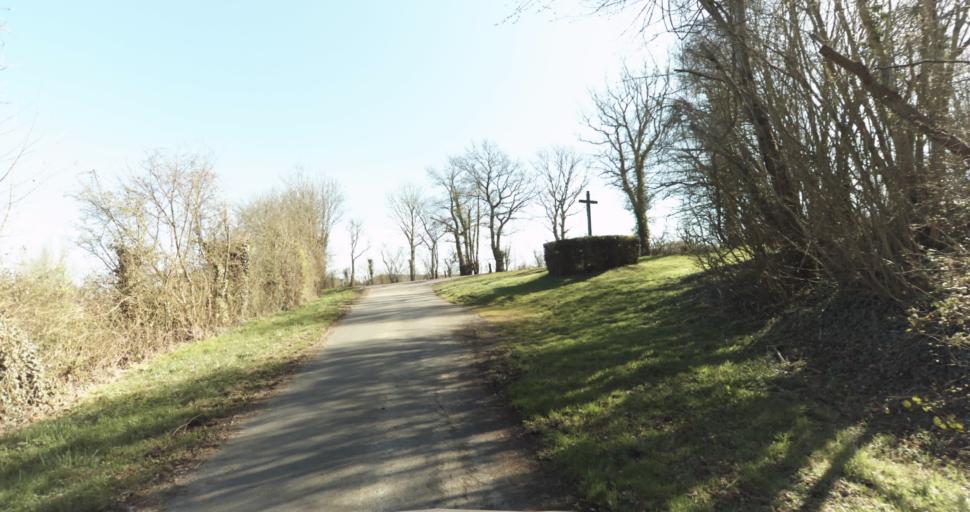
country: FR
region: Lower Normandy
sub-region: Departement de l'Orne
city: Trun
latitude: 48.9140
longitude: 0.0615
